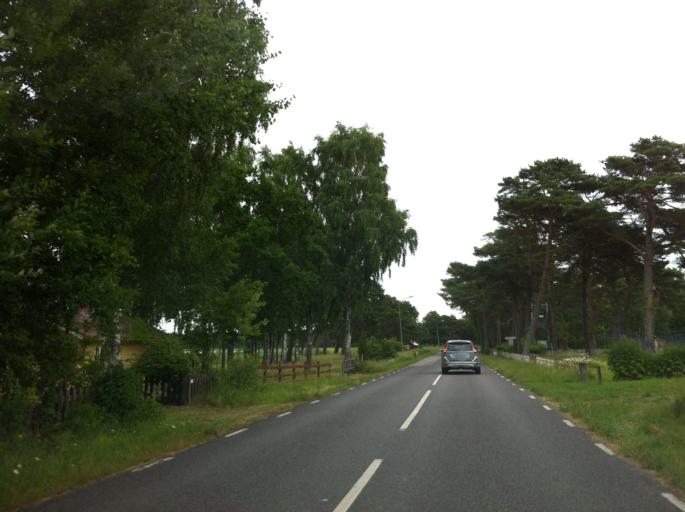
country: SE
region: Kalmar
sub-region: Vasterviks Kommun
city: Vaestervik
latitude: 57.3392
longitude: 17.0855
